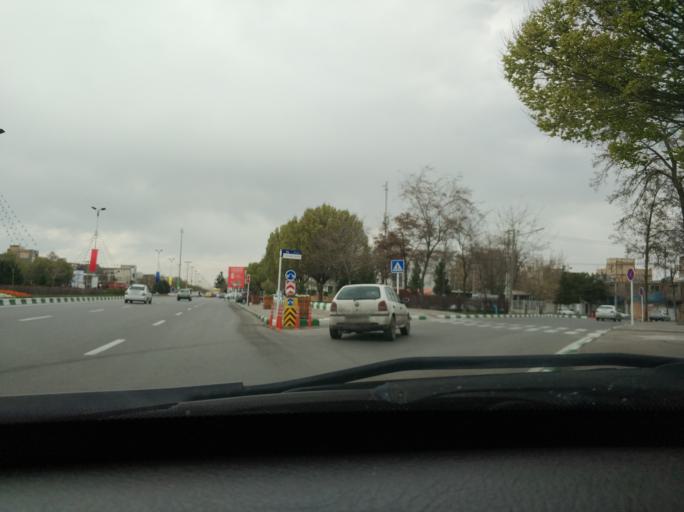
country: IR
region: Razavi Khorasan
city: Mashhad
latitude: 36.2565
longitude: 59.6105
